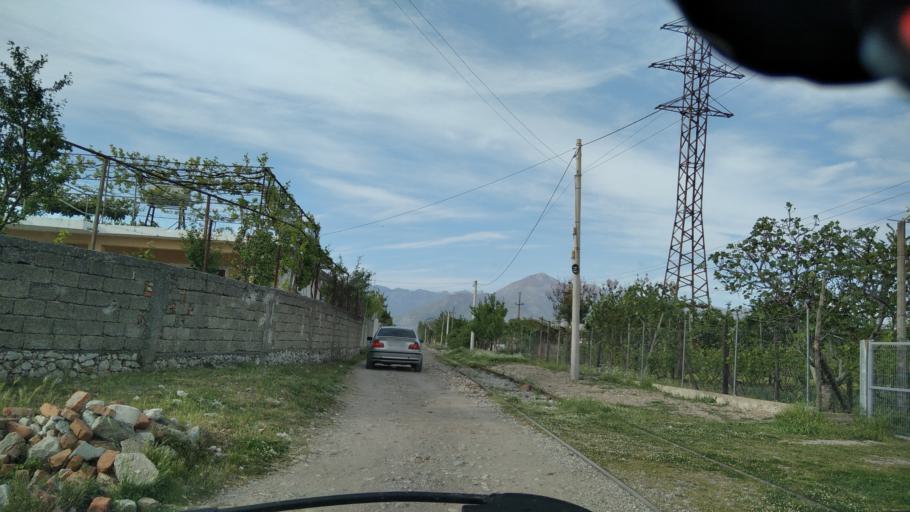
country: AL
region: Shkoder
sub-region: Rrethi i Shkodres
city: Shkoder
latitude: 42.0681
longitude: 19.5284
